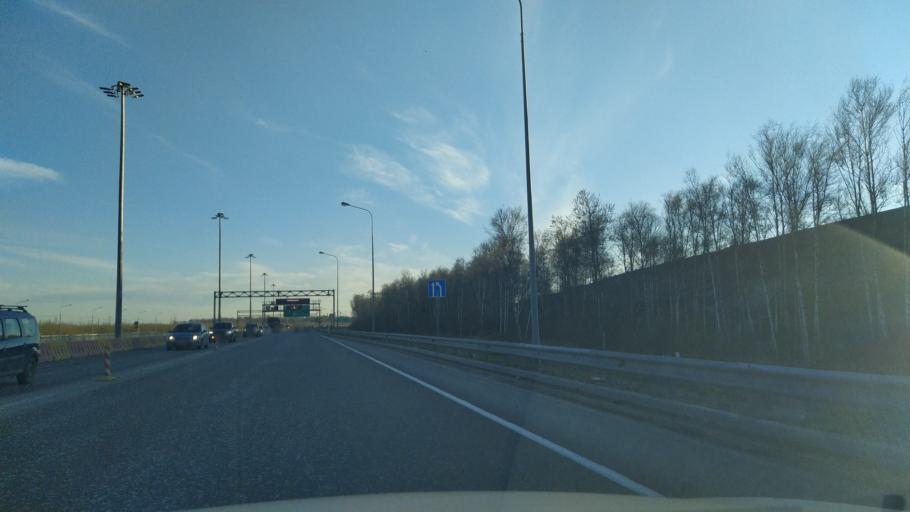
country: RU
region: St.-Petersburg
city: Levashovo
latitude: 60.0722
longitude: 30.1766
